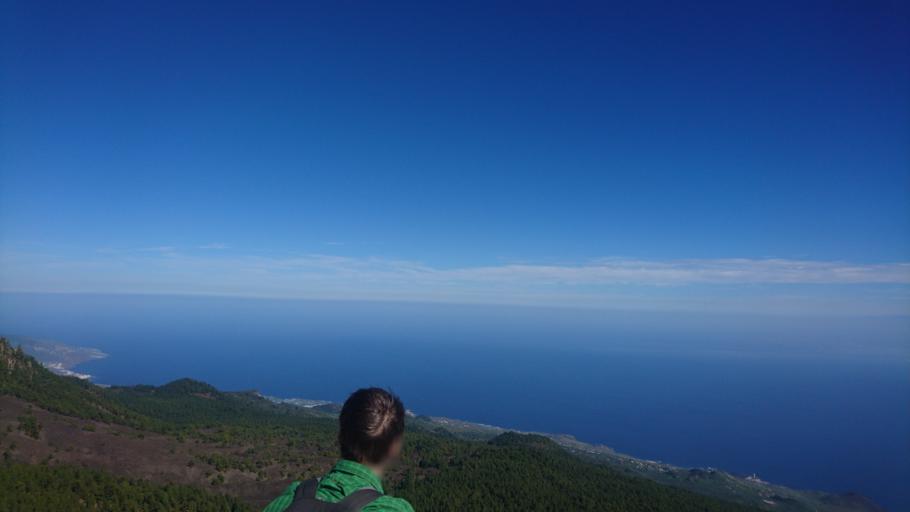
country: ES
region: Canary Islands
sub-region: Provincia de Santa Cruz de Tenerife
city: Mazo
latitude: 28.5692
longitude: -17.8372
